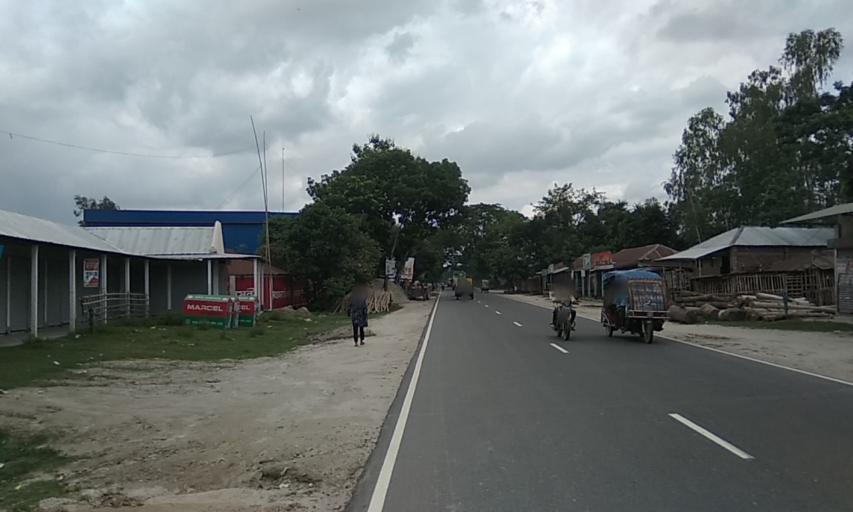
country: BD
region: Rangpur Division
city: Rangpur
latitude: 25.7983
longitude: 89.1934
